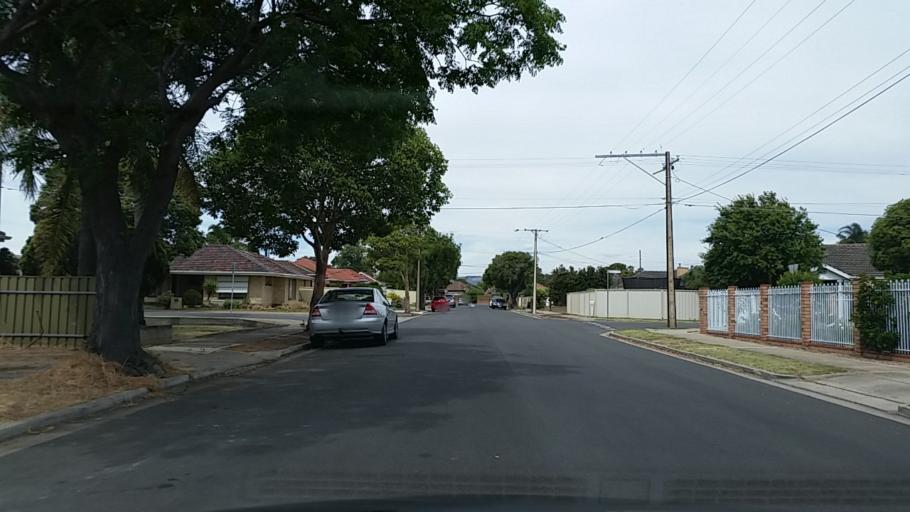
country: AU
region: South Australia
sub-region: City of West Torrens
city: Plympton
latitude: -34.9551
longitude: 138.5474
